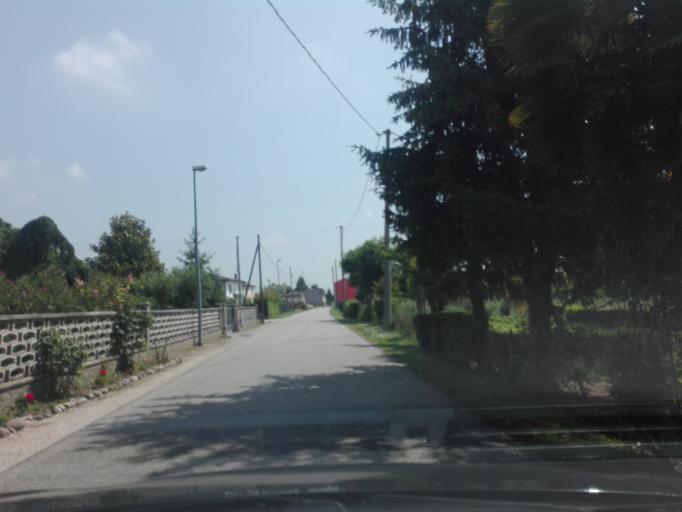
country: IT
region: Veneto
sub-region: Provincia di Rovigo
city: Villanova Marchesana
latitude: 45.0630
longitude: 11.9786
